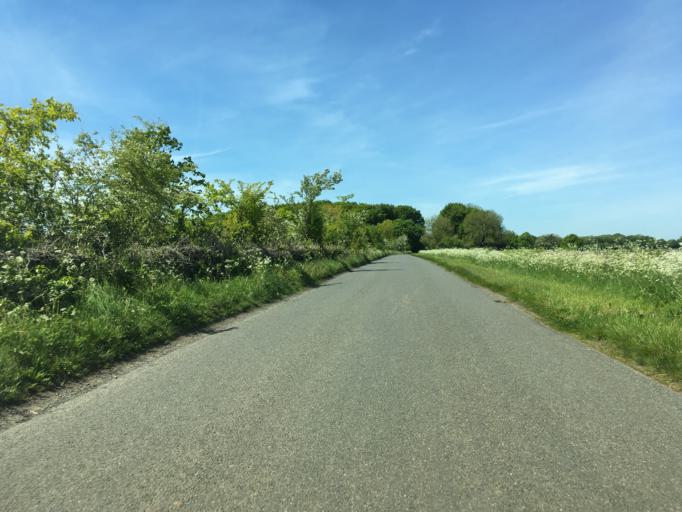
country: GB
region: England
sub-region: Gloucestershire
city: Coates
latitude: 51.6941
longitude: -2.0166
